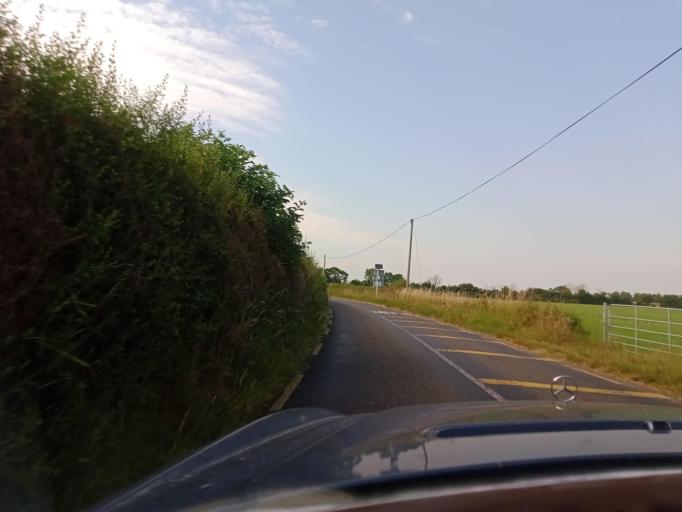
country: IE
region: Leinster
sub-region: Kilkenny
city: Callan
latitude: 52.5053
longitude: -7.3104
